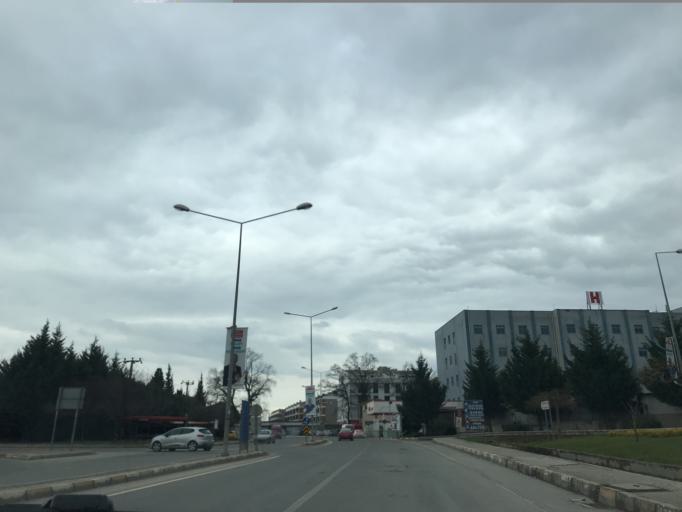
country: TR
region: Yalova
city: Ciftlikkoy
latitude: 40.6620
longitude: 29.3066
